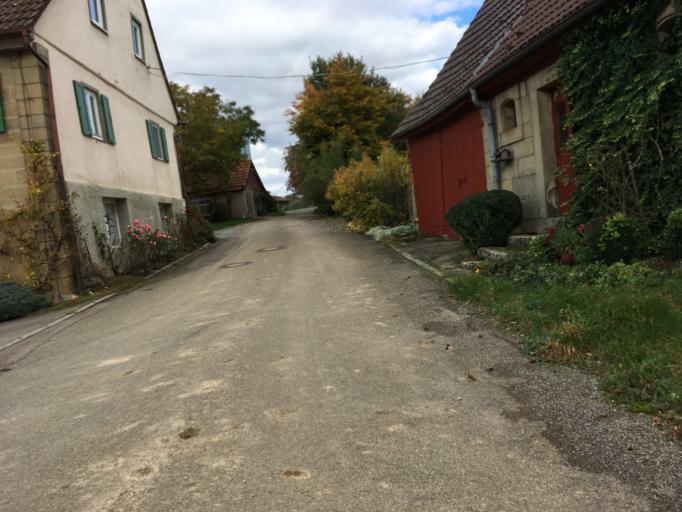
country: DE
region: Baden-Wuerttemberg
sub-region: Regierungsbezirk Stuttgart
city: Untermunkheim
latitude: 49.1899
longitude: 9.7419
